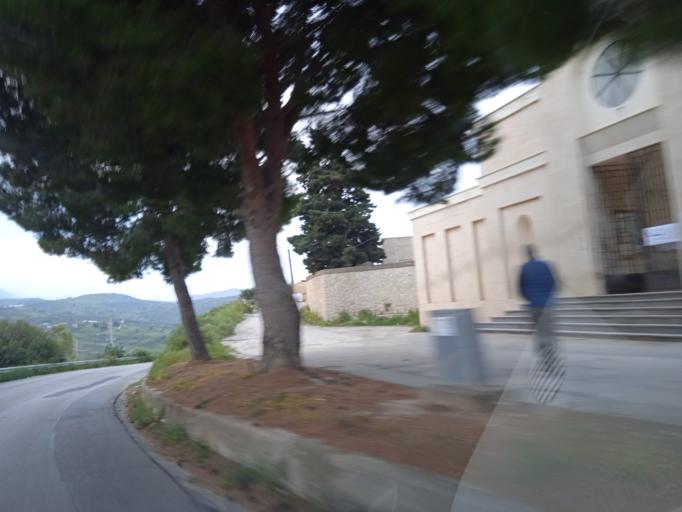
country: IT
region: Sicily
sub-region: Palermo
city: Portella di Mare
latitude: 38.0559
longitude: 13.4613
